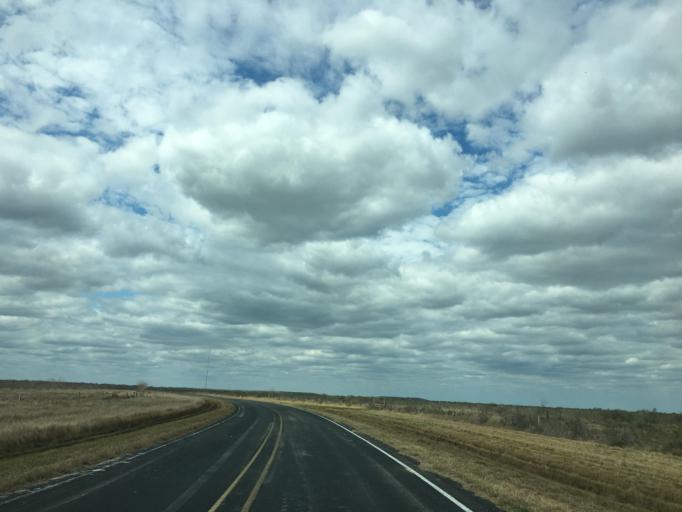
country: US
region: Texas
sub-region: Brazoria County
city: Oyster Creek
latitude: 29.0655
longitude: -95.2949
